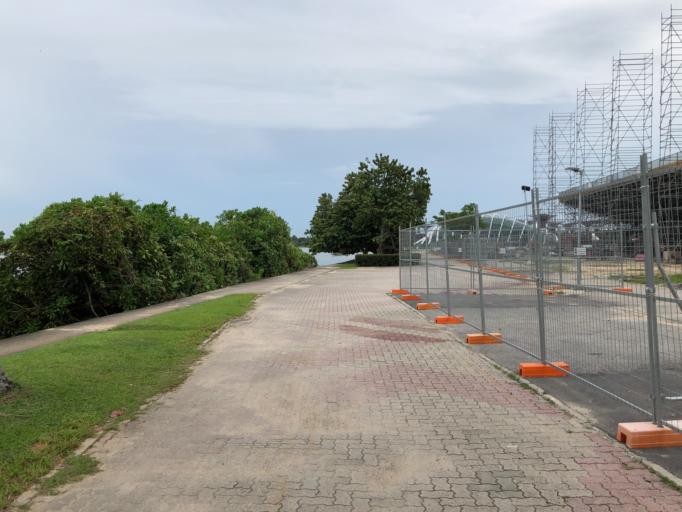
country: SG
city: Singapore
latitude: 1.2911
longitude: 103.8647
